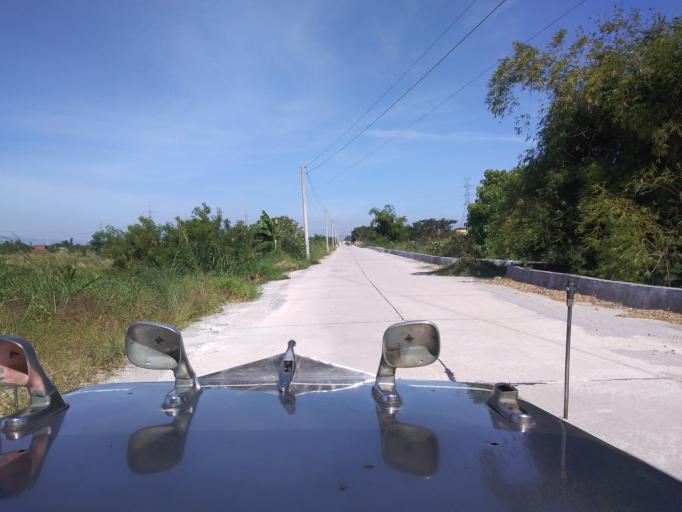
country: PH
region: Central Luzon
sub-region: Province of Pampanga
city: Bacolor
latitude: 15.0031
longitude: 120.6605
